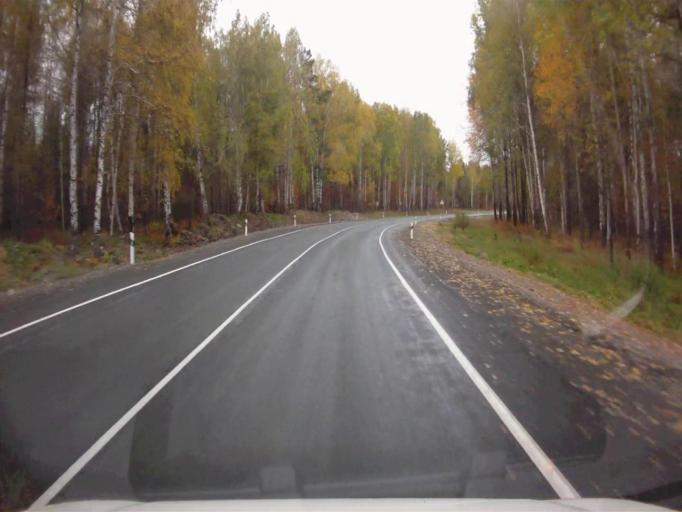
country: RU
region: Chelyabinsk
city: Nyazepetrovsk
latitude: 56.0606
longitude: 59.7304
